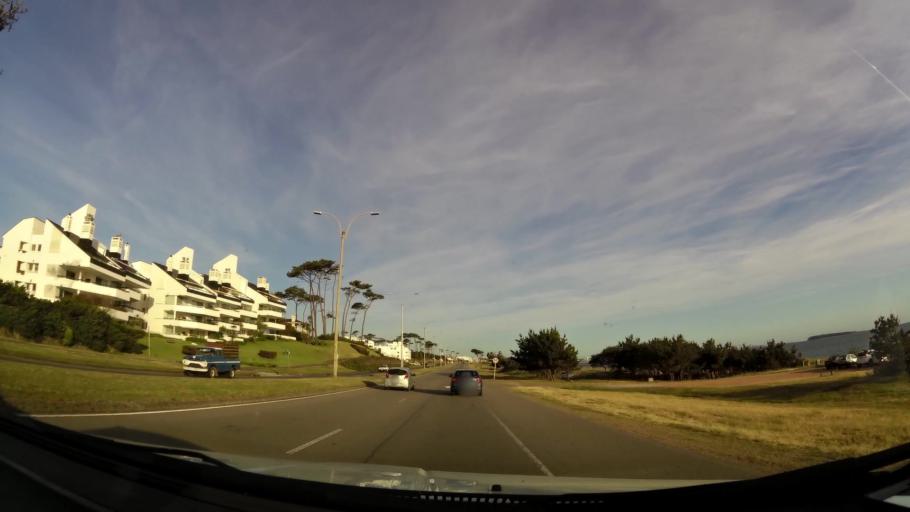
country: UY
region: Maldonado
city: Maldonado
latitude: -34.9113
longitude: -54.9926
